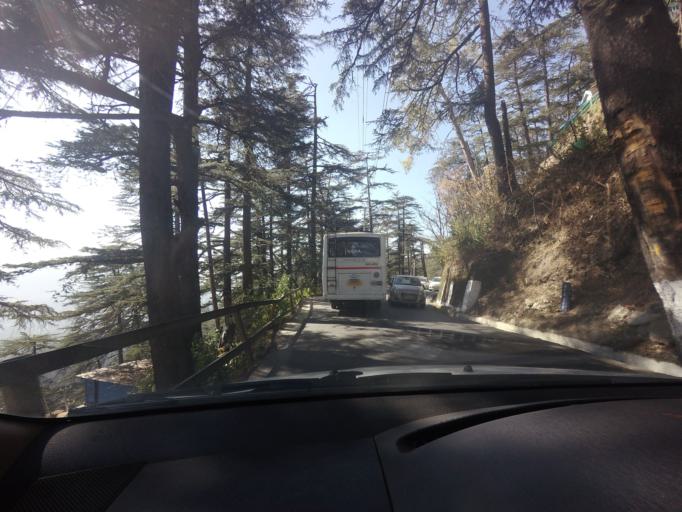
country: IN
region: Himachal Pradesh
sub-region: Shimla
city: Shimla
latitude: 31.1028
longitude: 77.1572
